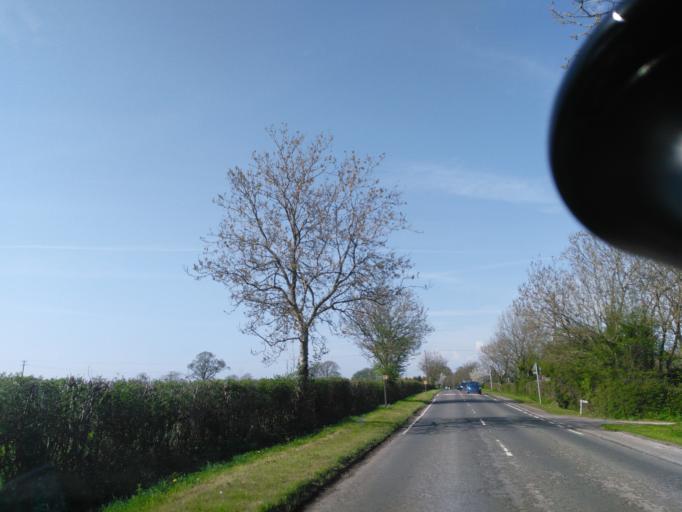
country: GB
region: England
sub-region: Wiltshire
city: Wingfield
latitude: 51.3105
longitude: -2.2571
